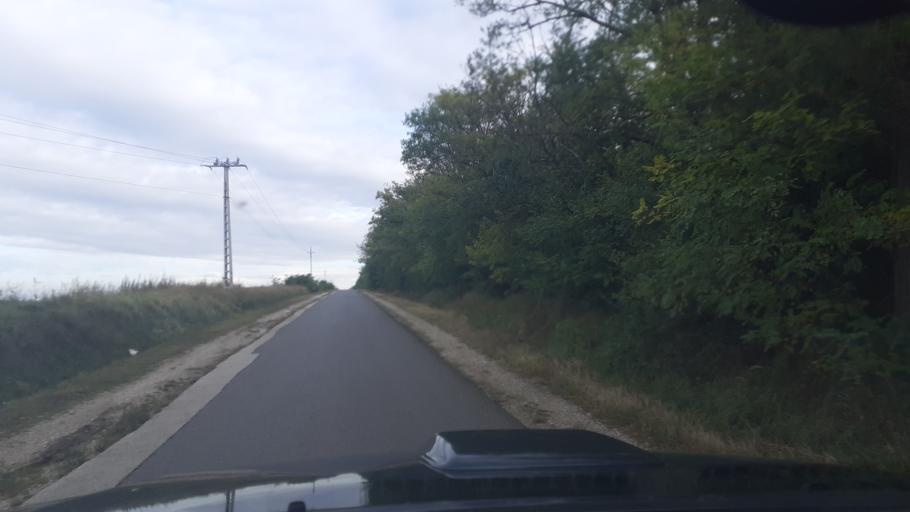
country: HU
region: Fejer
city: Baracs
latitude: 46.9284
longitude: 18.8743
